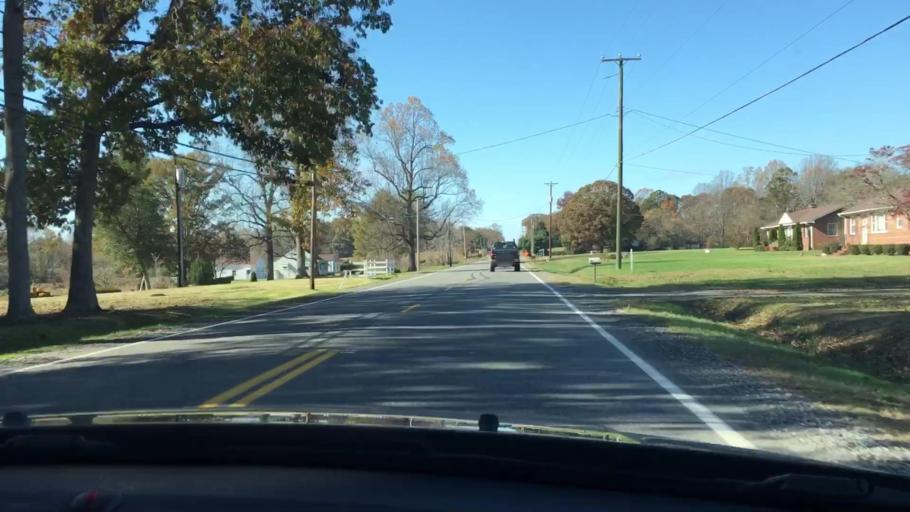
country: US
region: Virginia
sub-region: King William County
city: Central Garage
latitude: 37.7317
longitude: -77.1095
